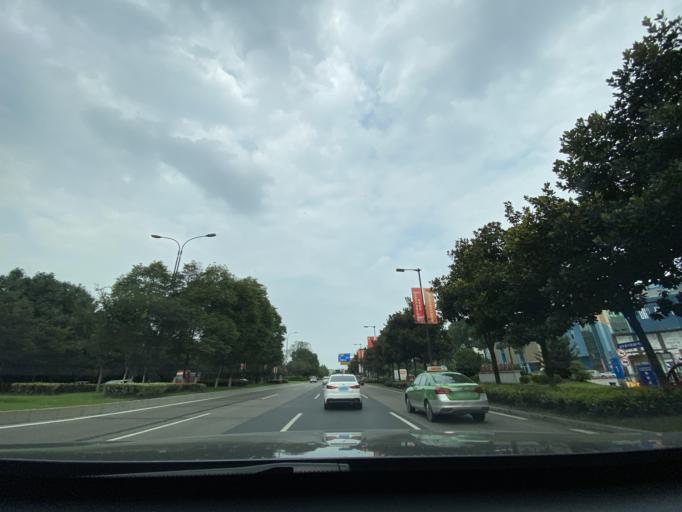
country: CN
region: Sichuan
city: Dongsheng
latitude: 30.6055
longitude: 103.9322
